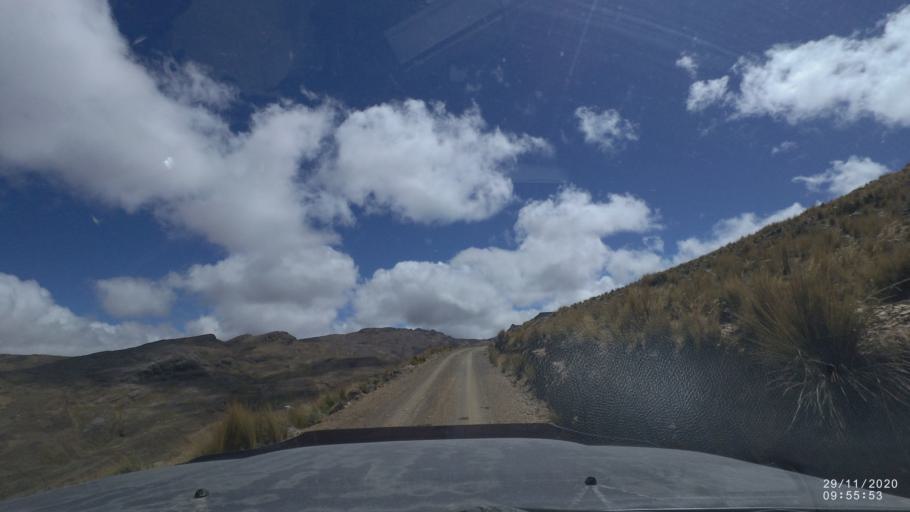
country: BO
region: Cochabamba
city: Cochabamba
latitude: -17.2733
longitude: -66.1768
